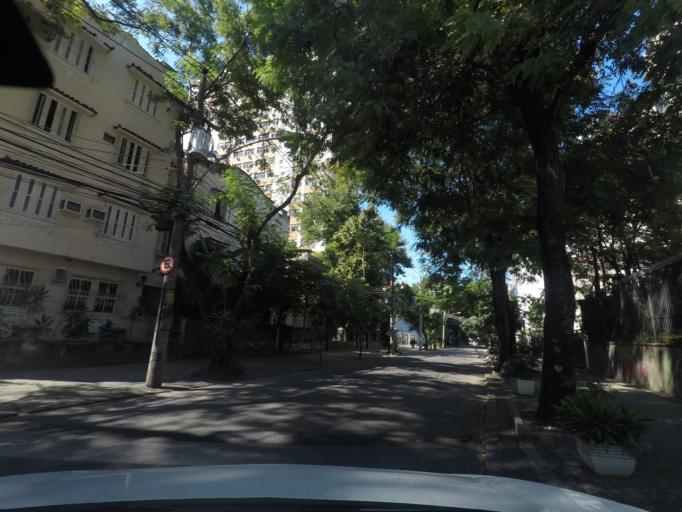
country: BR
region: Rio de Janeiro
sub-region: Rio De Janeiro
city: Rio de Janeiro
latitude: -22.9318
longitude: -43.2369
